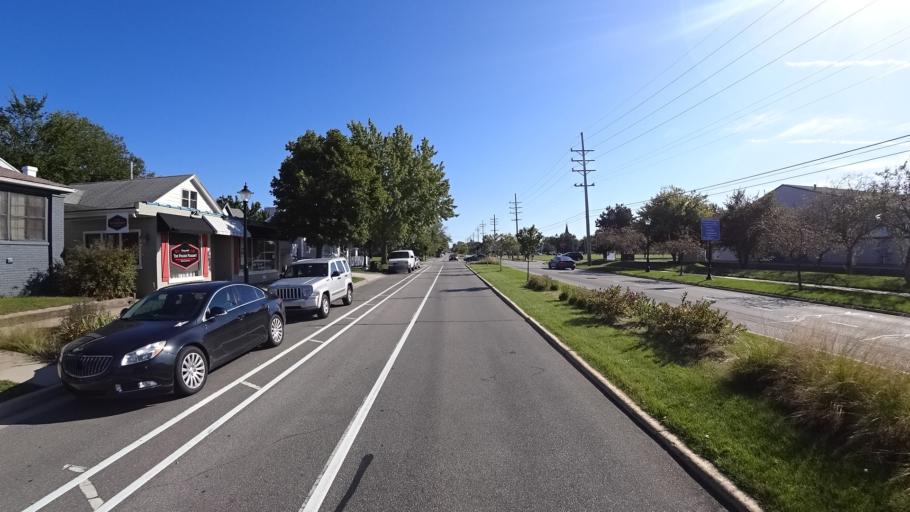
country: US
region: Indiana
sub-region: LaPorte County
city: Michigan City
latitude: 41.7143
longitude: -86.9037
